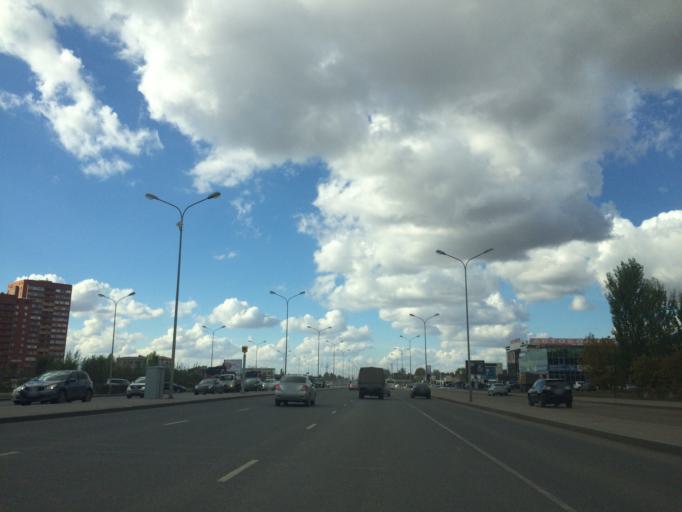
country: KZ
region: Astana Qalasy
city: Astana
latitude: 51.1806
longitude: 71.3785
